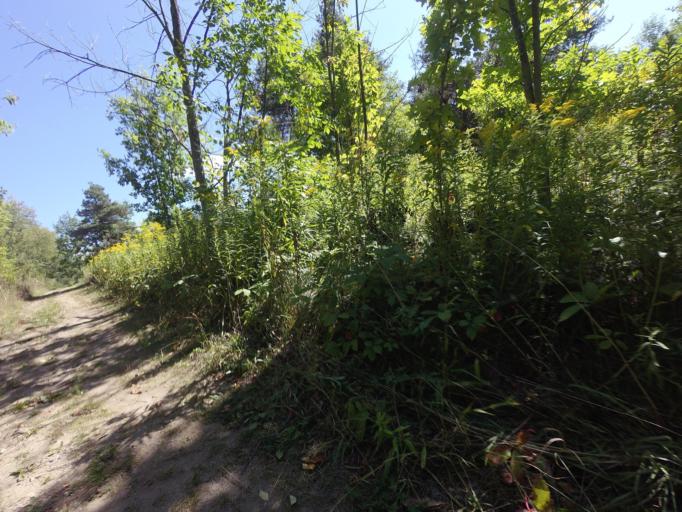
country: CA
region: Ontario
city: Orangeville
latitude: 43.8207
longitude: -80.0148
